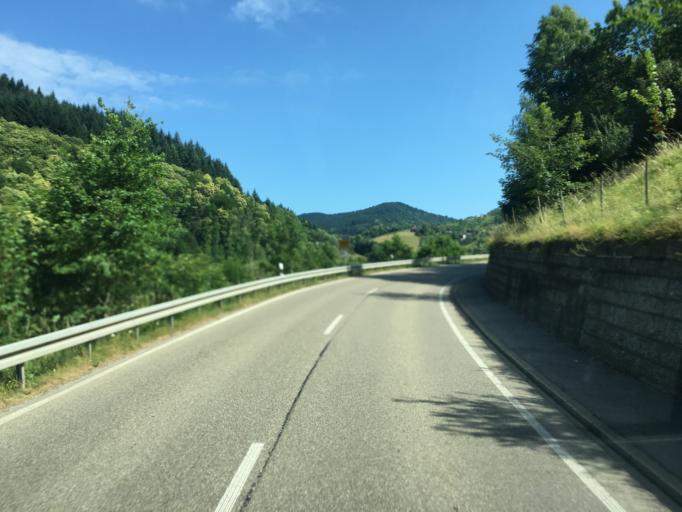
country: DE
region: Baden-Wuerttemberg
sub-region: Freiburg Region
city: Seebach
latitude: 48.5740
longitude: 8.1651
